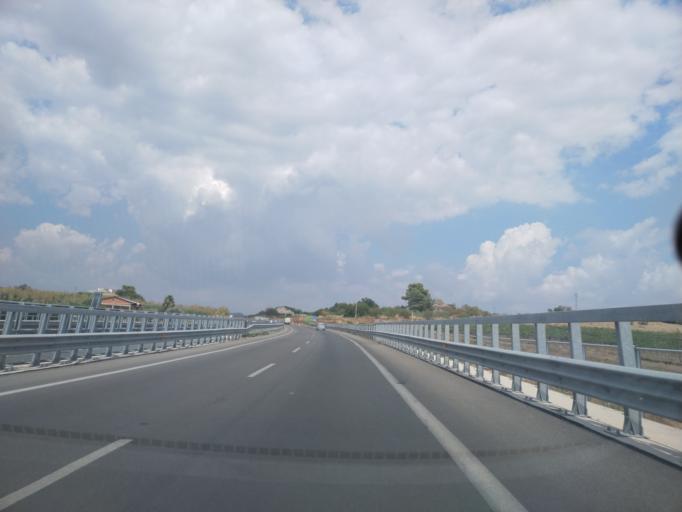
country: IT
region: Sicily
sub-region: Agrigento
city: Grotte
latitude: 37.3629
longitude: 13.7019
